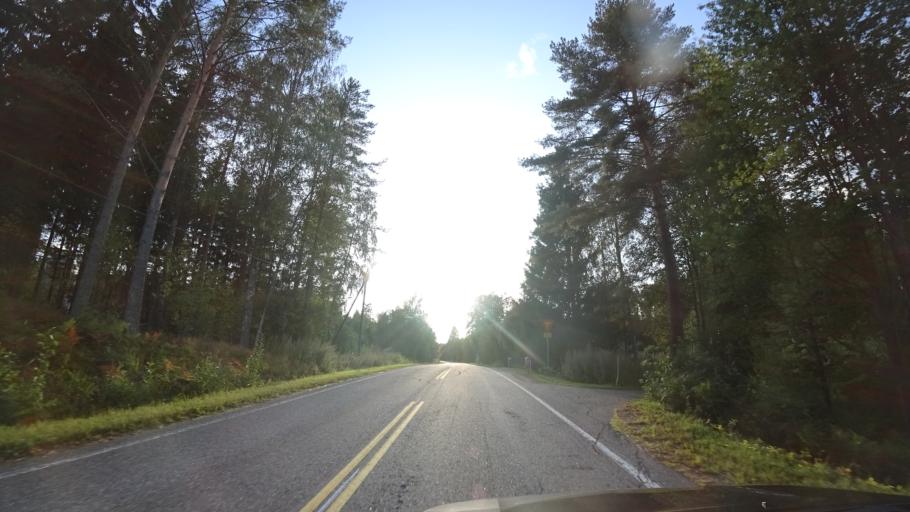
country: FI
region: Haeme
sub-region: Haemeenlinna
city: Lammi
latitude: 61.0632
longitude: 24.9845
